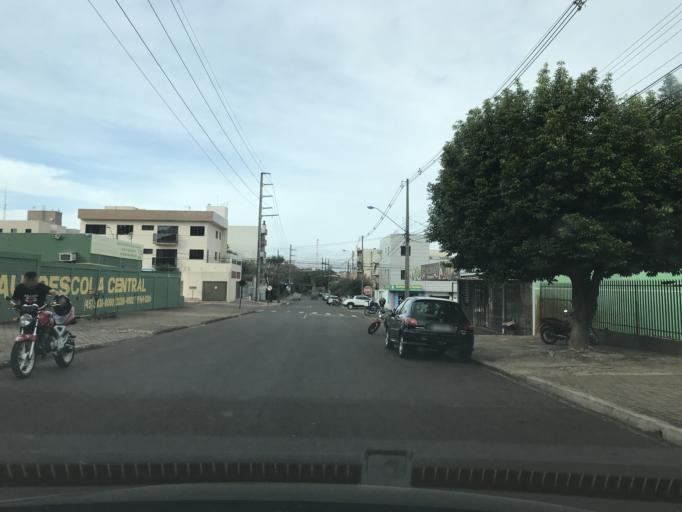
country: BR
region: Parana
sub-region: Cascavel
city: Cascavel
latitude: -24.9548
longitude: -53.4816
